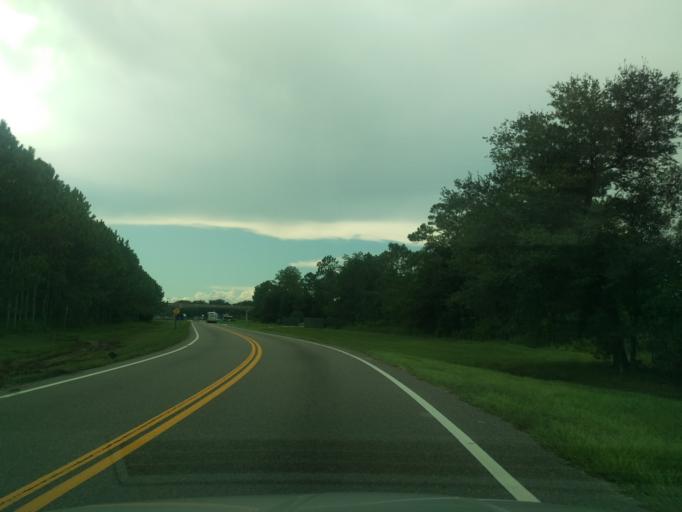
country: US
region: Florida
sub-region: Osceola County
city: Celebration
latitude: 28.3947
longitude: -81.5680
